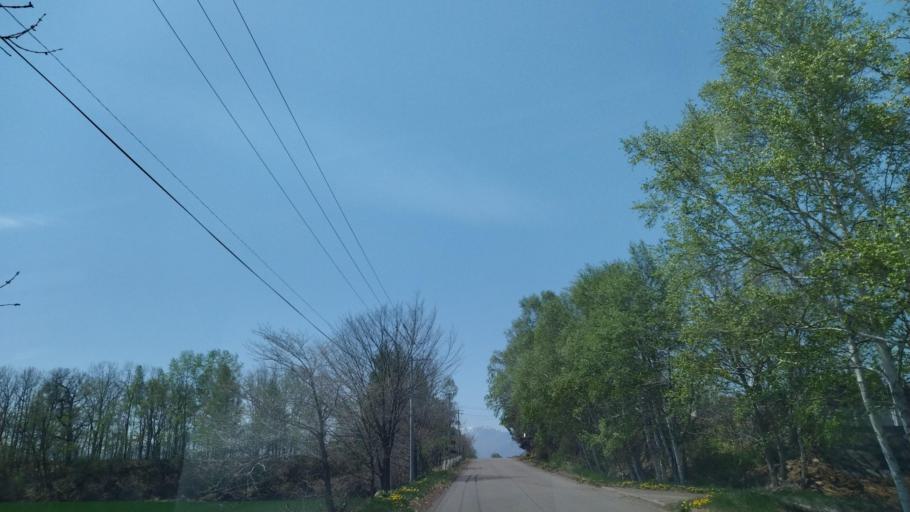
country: JP
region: Hokkaido
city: Obihiro
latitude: 42.8941
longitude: 143.0266
